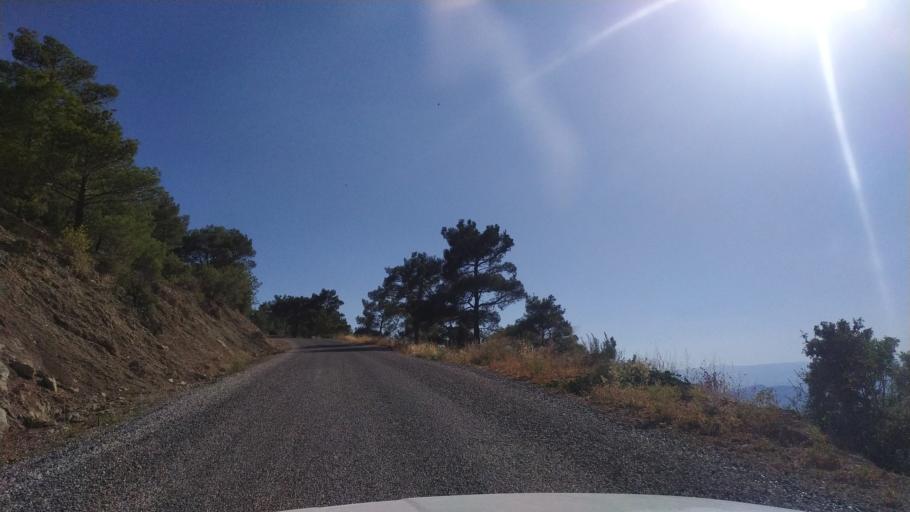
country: TR
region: Mersin
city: Mut
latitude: 36.7037
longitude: 33.4728
